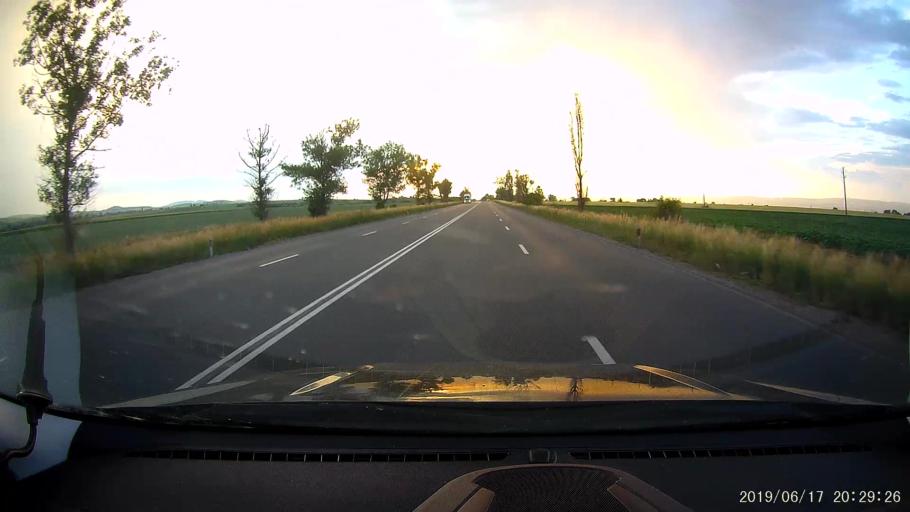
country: BG
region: Sofiya
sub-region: Obshtina Bozhurishte
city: Bozhurishte
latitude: 42.7862
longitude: 23.1620
